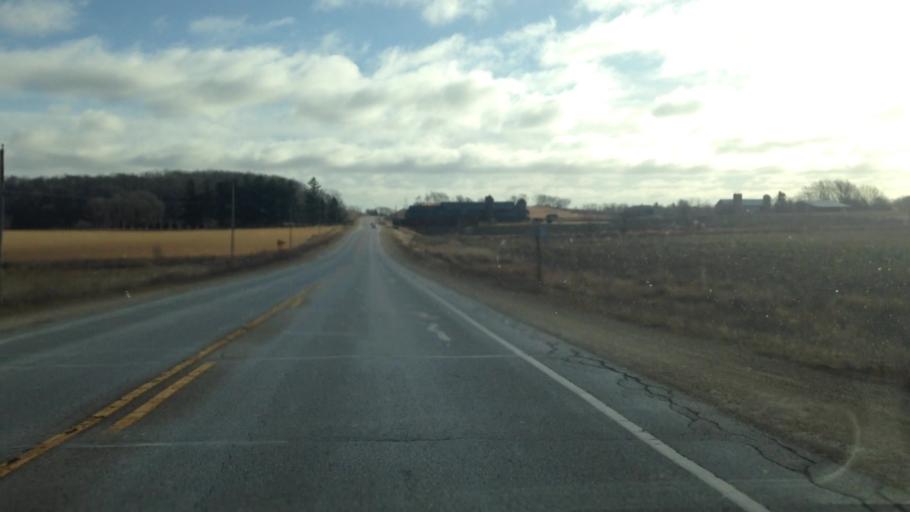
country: US
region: Wisconsin
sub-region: Dodge County
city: Theresa
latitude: 43.4349
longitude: -88.4669
